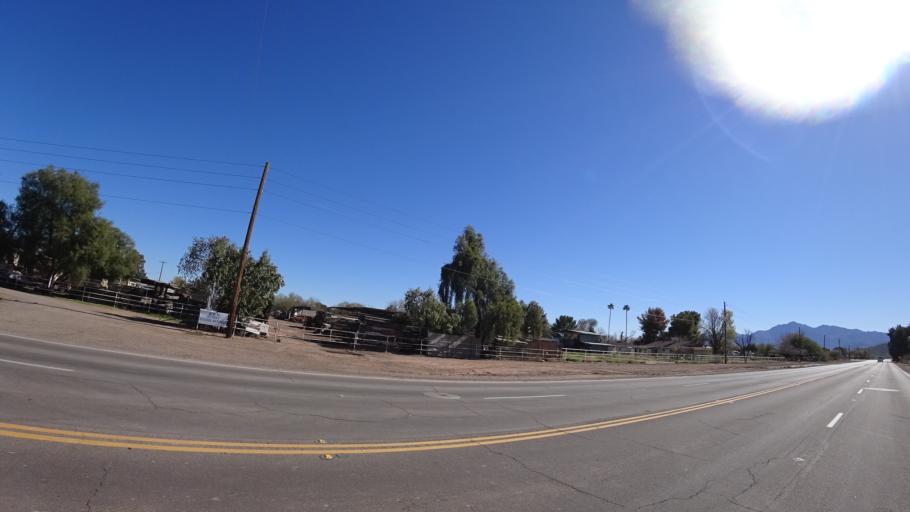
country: US
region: Arizona
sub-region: Maricopa County
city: Avondale
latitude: 33.3954
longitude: -112.3062
